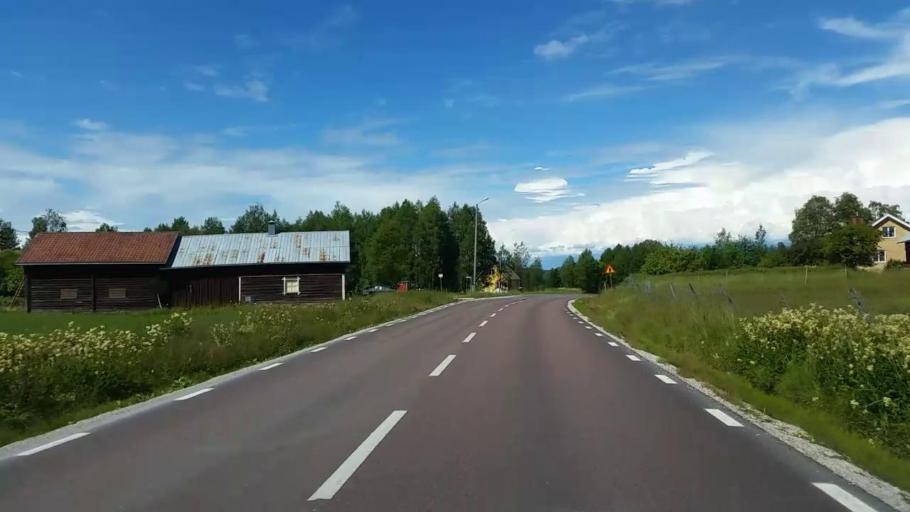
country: SE
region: Dalarna
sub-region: Rattviks Kommun
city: Raettvik
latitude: 61.0403
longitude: 15.1963
